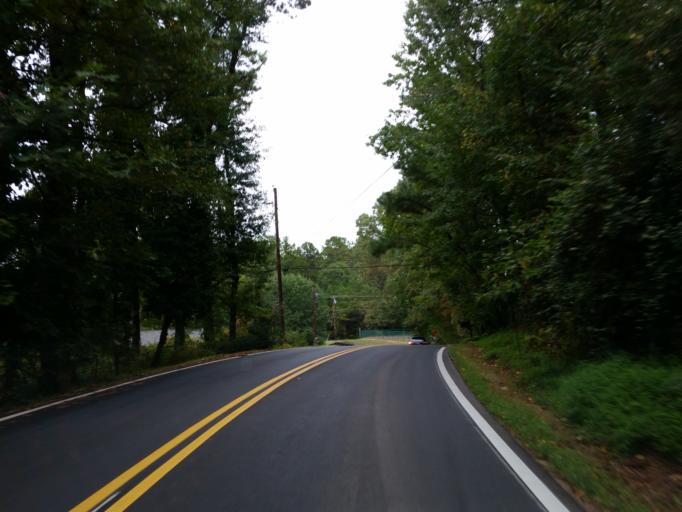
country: US
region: Georgia
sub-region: Cherokee County
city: Woodstock
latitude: 34.0353
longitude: -84.5078
